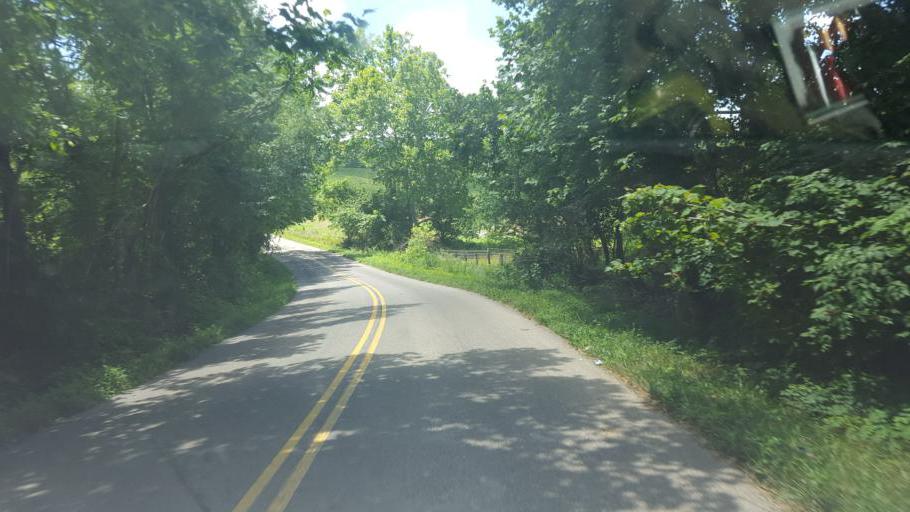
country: US
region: Ohio
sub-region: Gallia County
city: Gallipolis
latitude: 38.7522
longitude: -82.3721
